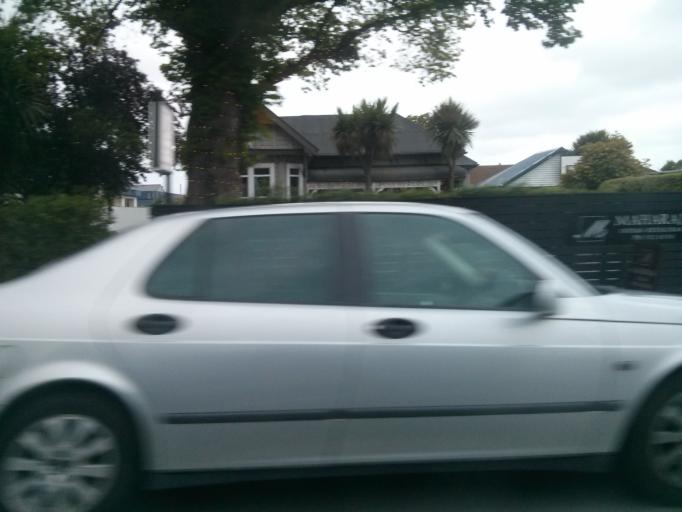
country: NZ
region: Canterbury
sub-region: Christchurch City
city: Christchurch
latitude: -43.4994
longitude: 172.6101
